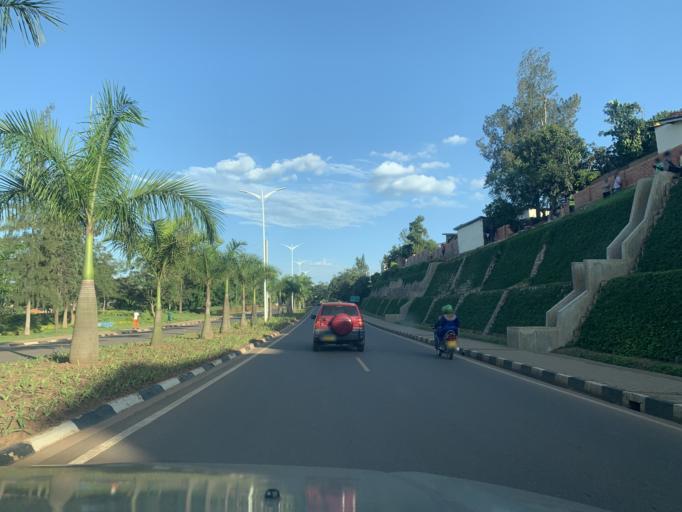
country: RW
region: Kigali
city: Kigali
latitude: -1.9630
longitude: 30.1255
